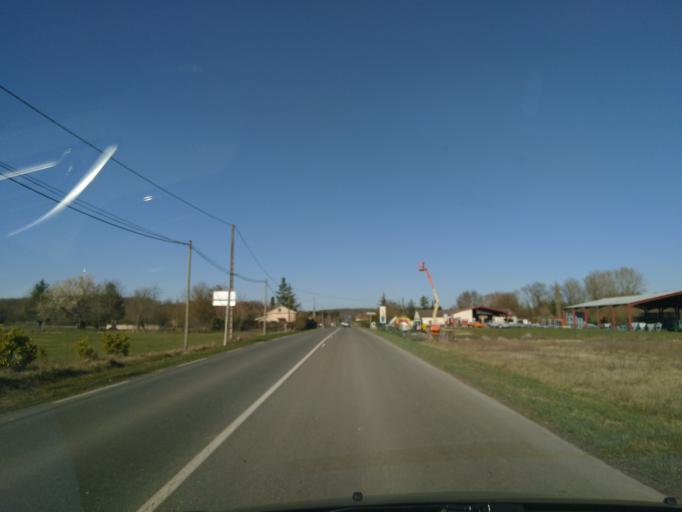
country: FR
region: Aquitaine
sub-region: Departement du Lot-et-Garonne
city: Castillonnes
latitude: 44.7065
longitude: 0.5621
